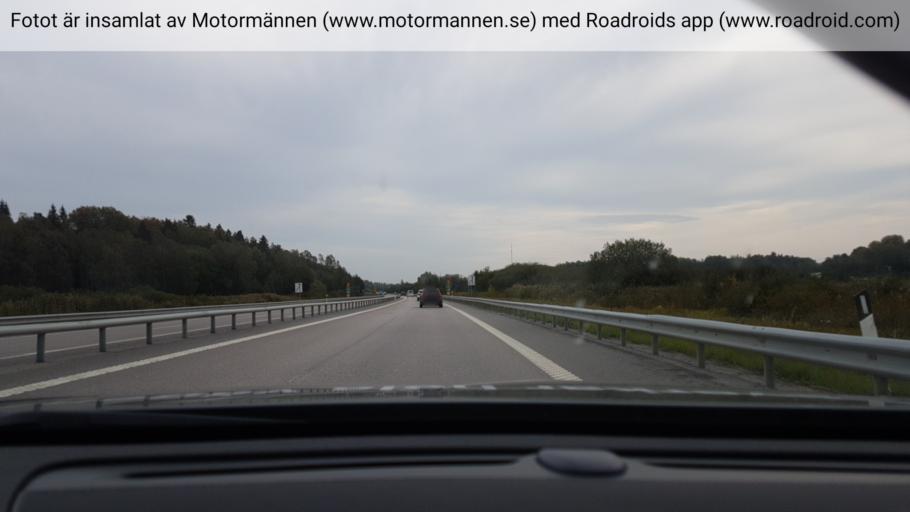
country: SE
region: Stockholm
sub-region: Nynashamns Kommun
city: Nynashamn
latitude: 58.9367
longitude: 17.9204
